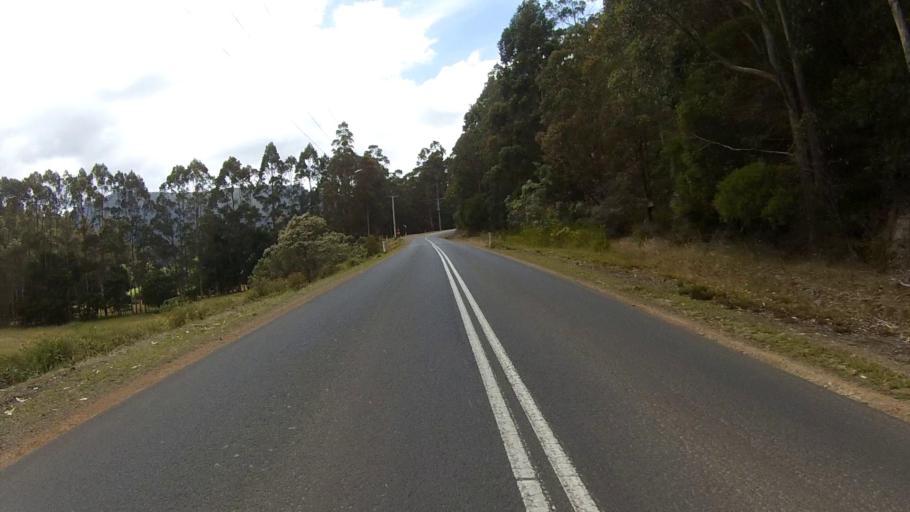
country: AU
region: Tasmania
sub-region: Huon Valley
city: Cygnet
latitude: -43.1322
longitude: 147.1564
